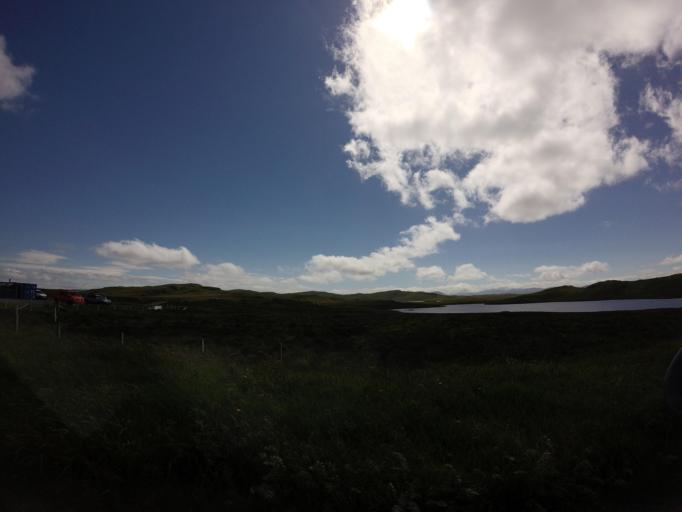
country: GB
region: Scotland
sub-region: Eilean Siar
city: Stornoway
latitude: 58.1582
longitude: -6.5240
